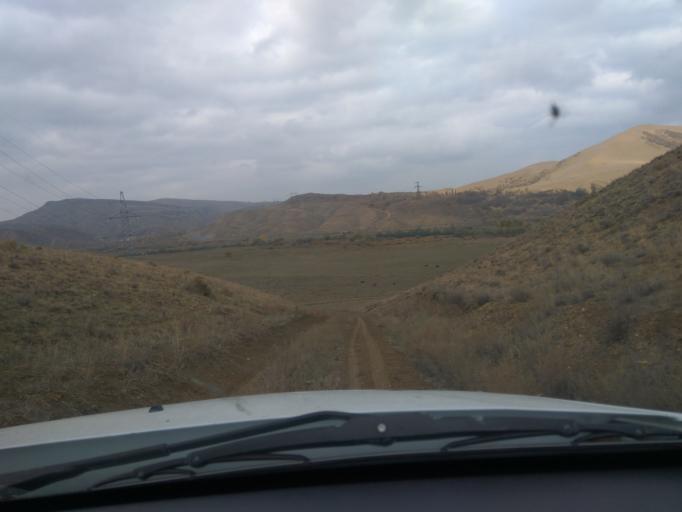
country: RU
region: Dagestan
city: Korkmaskala
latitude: 42.9940
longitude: 47.2327
